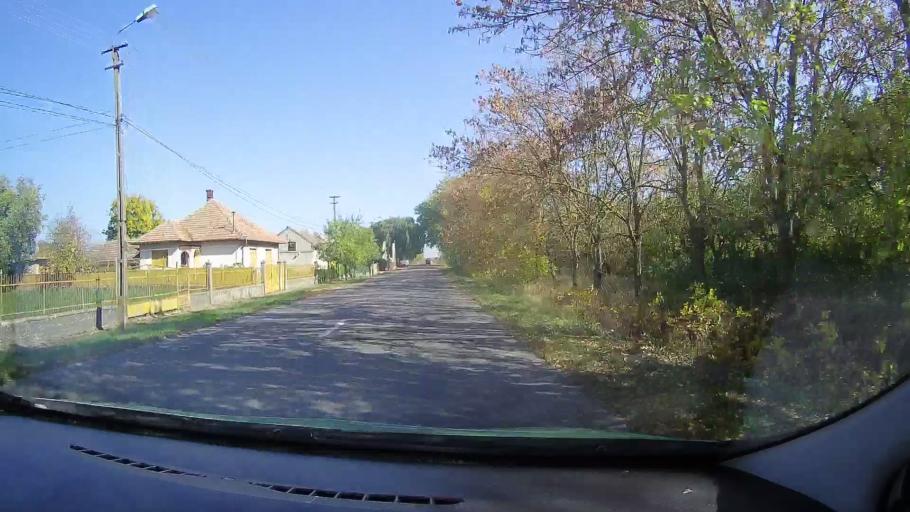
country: RO
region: Satu Mare
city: Carei
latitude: 47.6945
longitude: 22.4764
